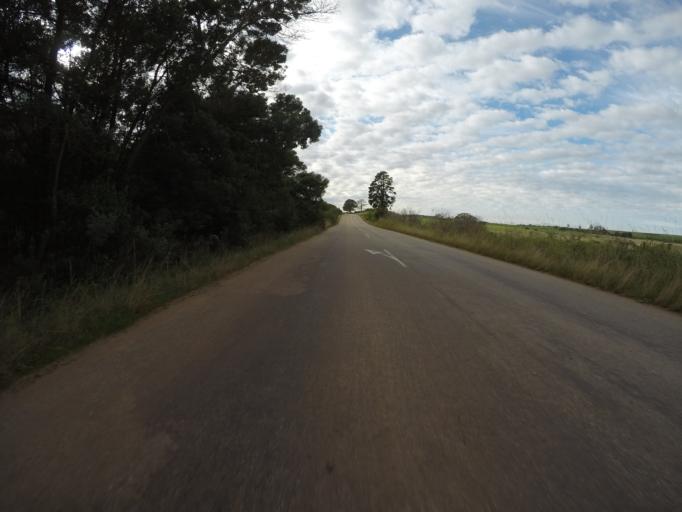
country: ZA
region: Eastern Cape
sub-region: Cacadu District Municipality
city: Kareedouw
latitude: -34.0092
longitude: 24.2706
